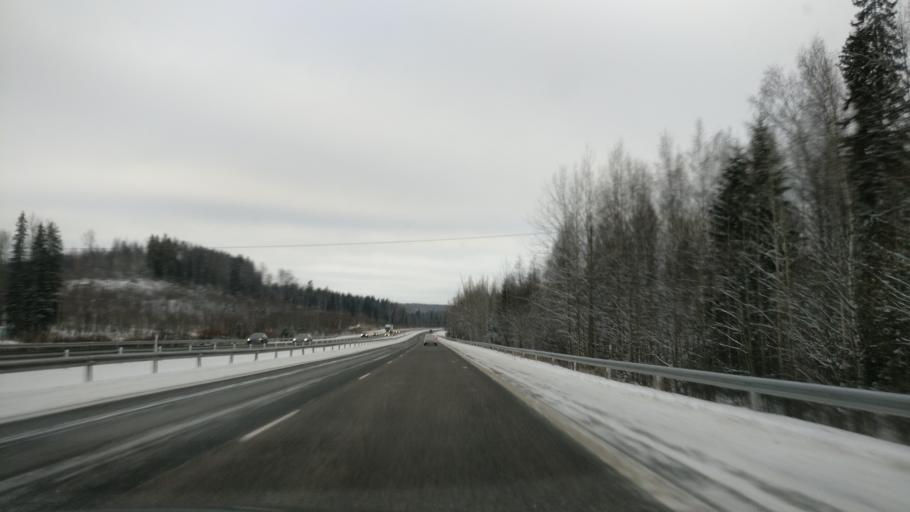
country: FI
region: Paijanne Tavastia
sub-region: Lahti
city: Lahti
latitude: 60.9571
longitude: 25.6975
